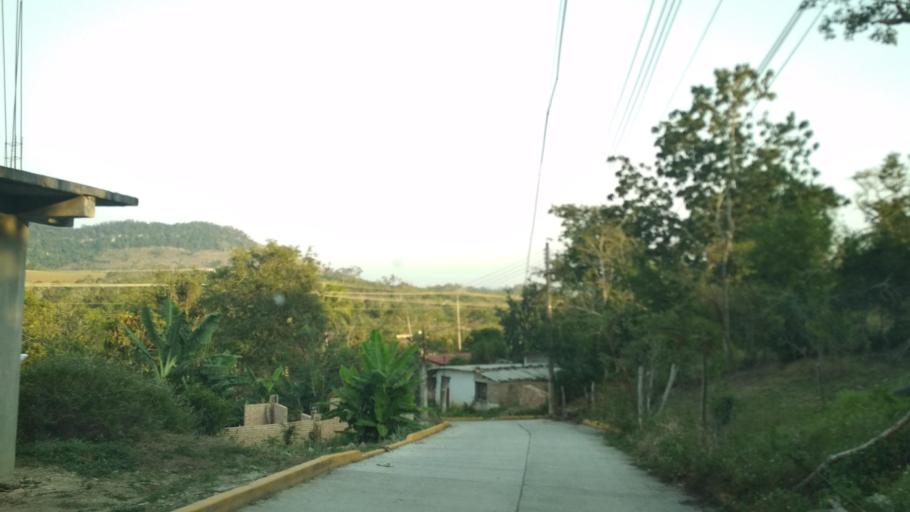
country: MM
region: Shan
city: Taunggyi
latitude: 20.4093
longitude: 97.3380
